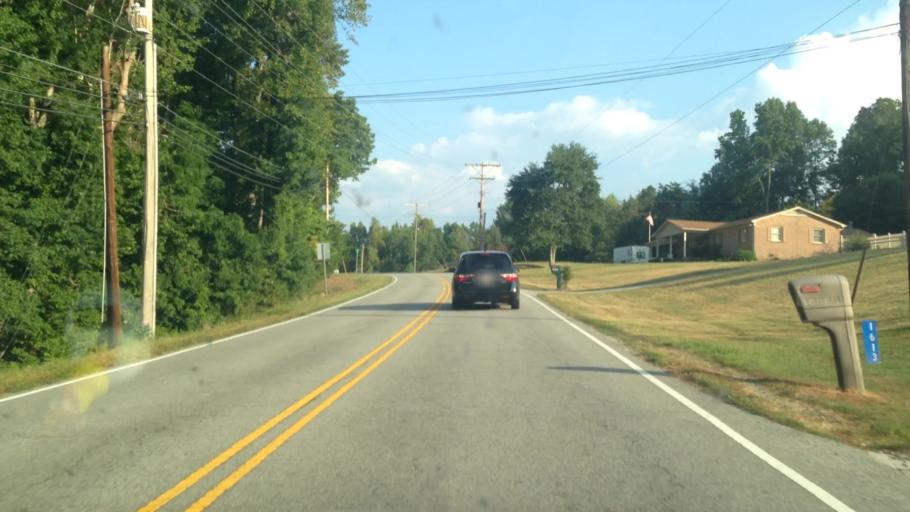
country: US
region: North Carolina
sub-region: Davidson County
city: Thomasville
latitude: 35.9434
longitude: -80.0746
